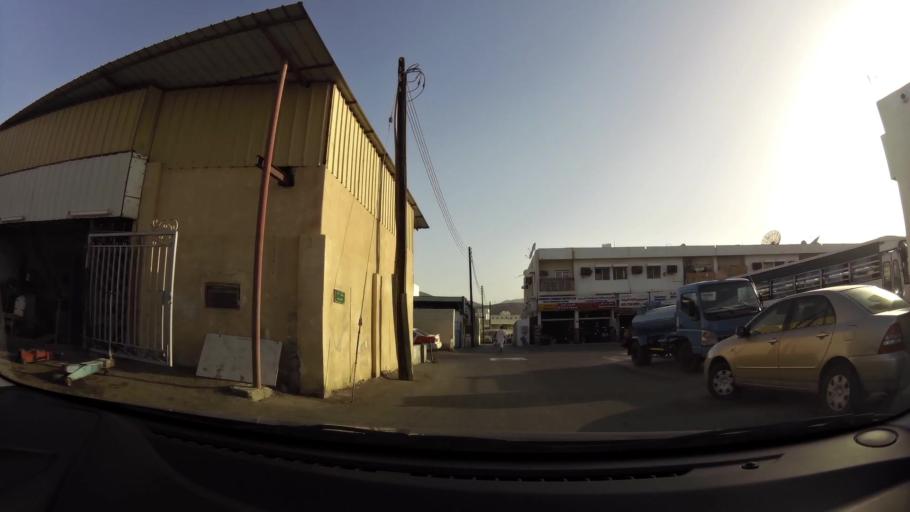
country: OM
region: Muhafazat Masqat
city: Muscat
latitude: 23.5895
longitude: 58.5547
